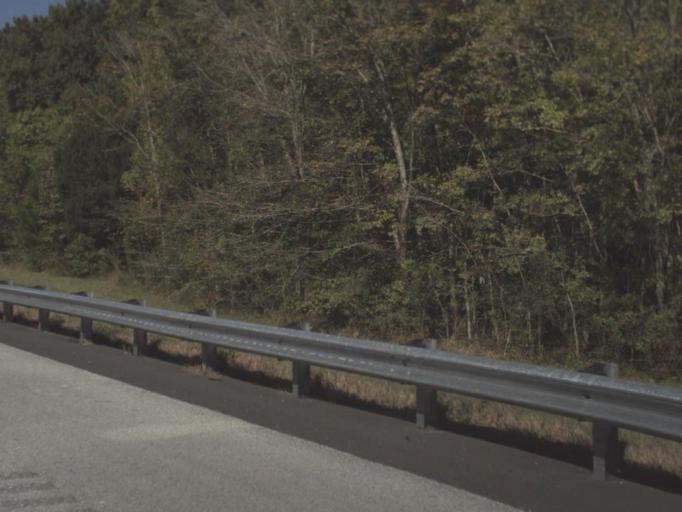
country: US
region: Florida
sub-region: Sumter County
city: Wildwood
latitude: 28.8417
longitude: -82.0578
